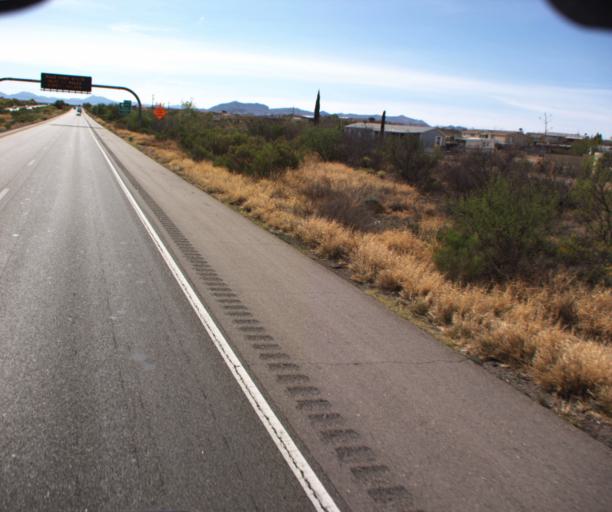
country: US
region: Arizona
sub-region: Pima County
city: Vail
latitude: 32.0154
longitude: -110.7032
